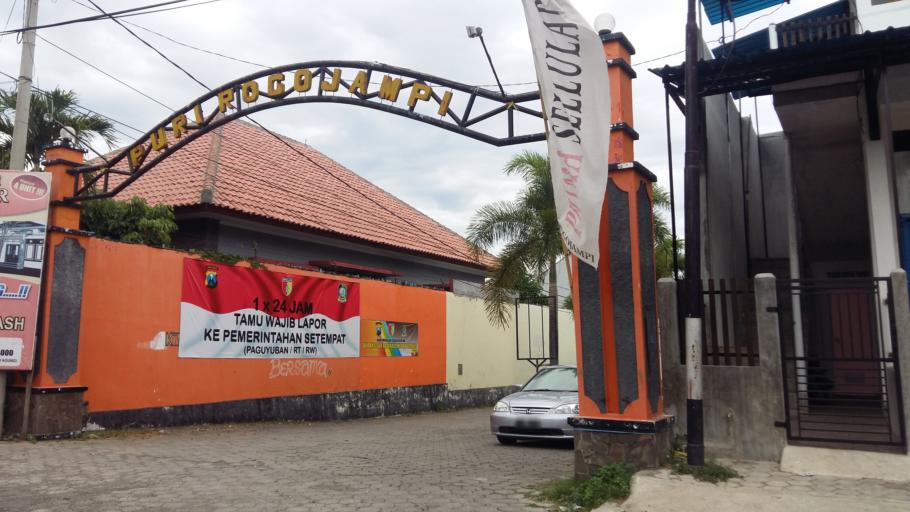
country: ID
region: East Java
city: Krajan
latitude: -8.3123
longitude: 114.2960
